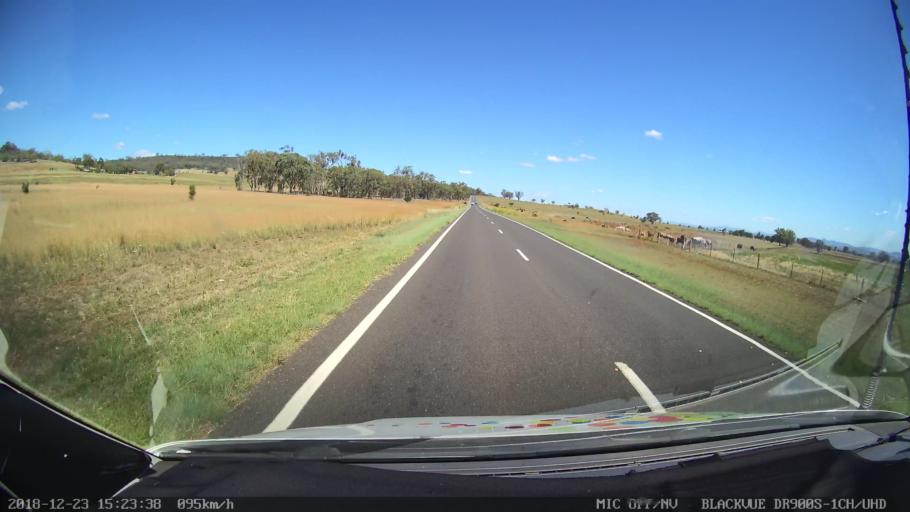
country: AU
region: New South Wales
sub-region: Tamworth Municipality
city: Manilla
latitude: -30.8823
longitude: 150.8159
